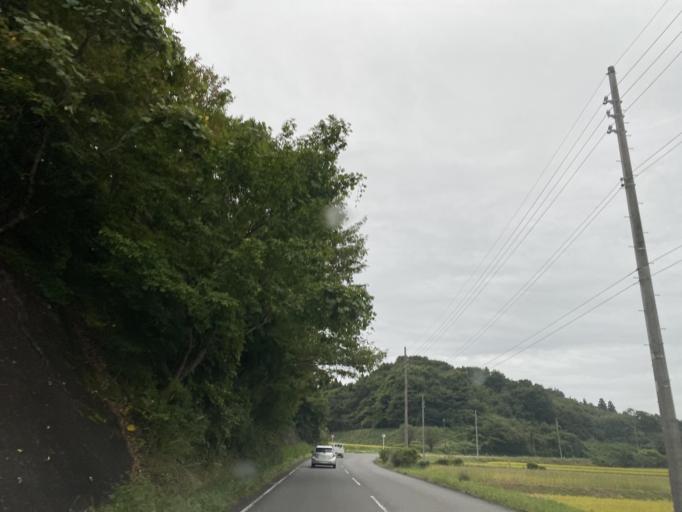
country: JP
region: Fukushima
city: Sukagawa
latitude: 37.3020
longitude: 140.2533
